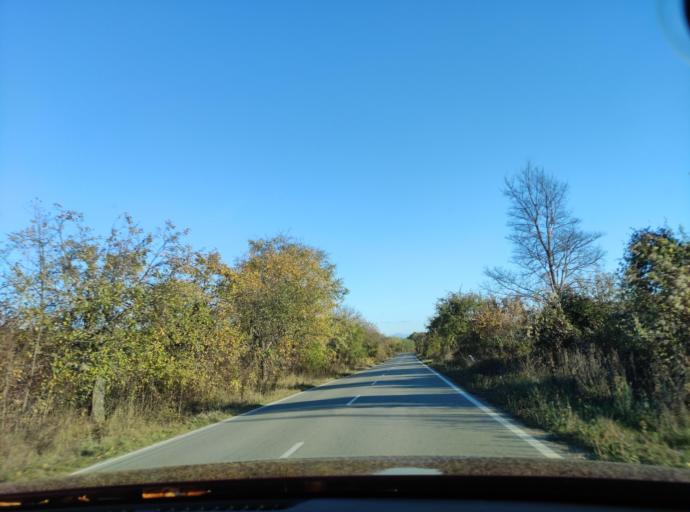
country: BG
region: Montana
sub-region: Obshtina Chiprovtsi
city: Chiprovtsi
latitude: 43.4213
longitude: 23.0182
